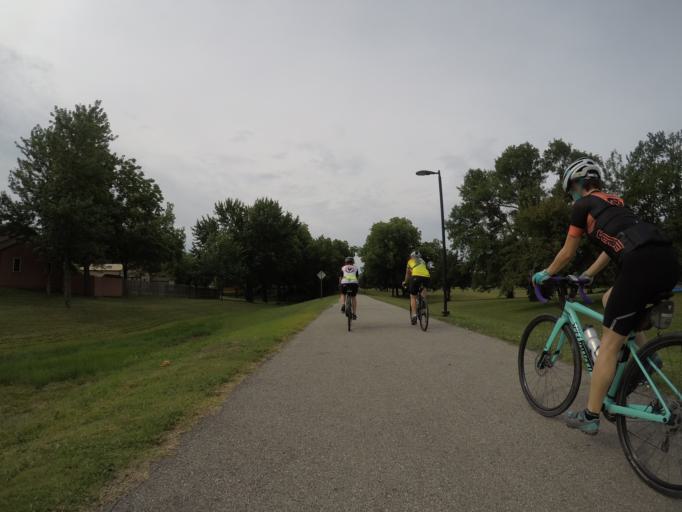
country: US
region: Kansas
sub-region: Franklin County
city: Ottawa
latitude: 38.6009
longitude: -95.2702
